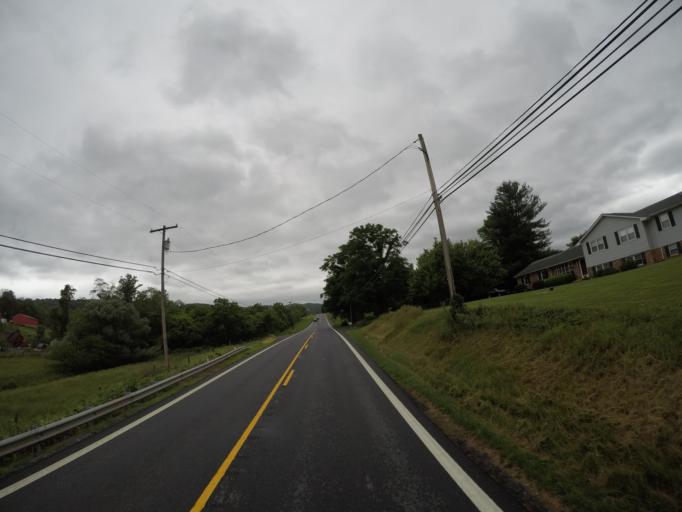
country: US
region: Maryland
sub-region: Frederick County
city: Myersville
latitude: 39.4687
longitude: -77.5958
